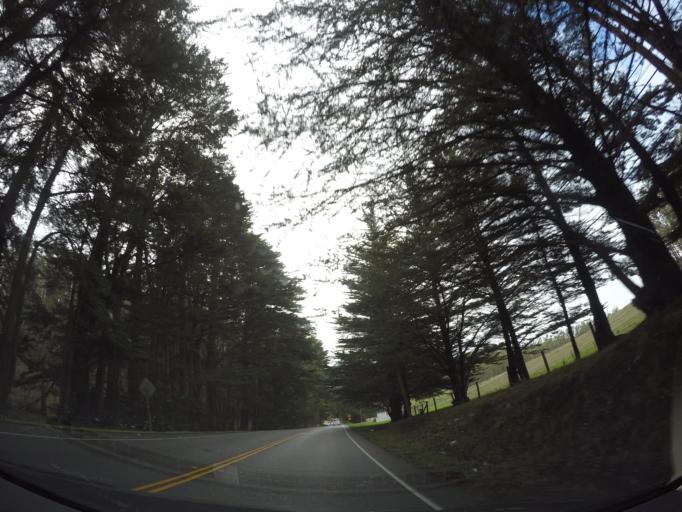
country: US
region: California
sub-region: Sonoma County
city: Bodega Bay
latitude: 38.3358
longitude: -122.9899
